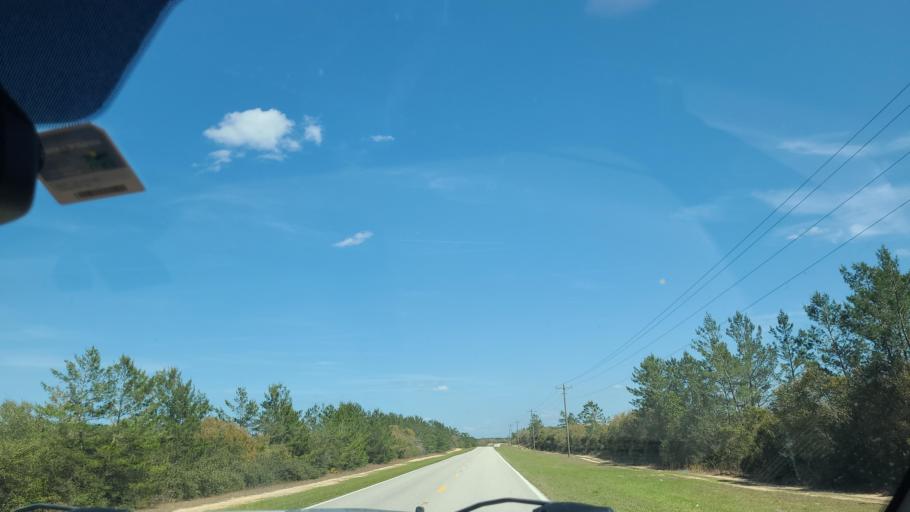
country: US
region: Florida
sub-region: Putnam County
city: Interlachen
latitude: 29.3685
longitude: -81.8486
